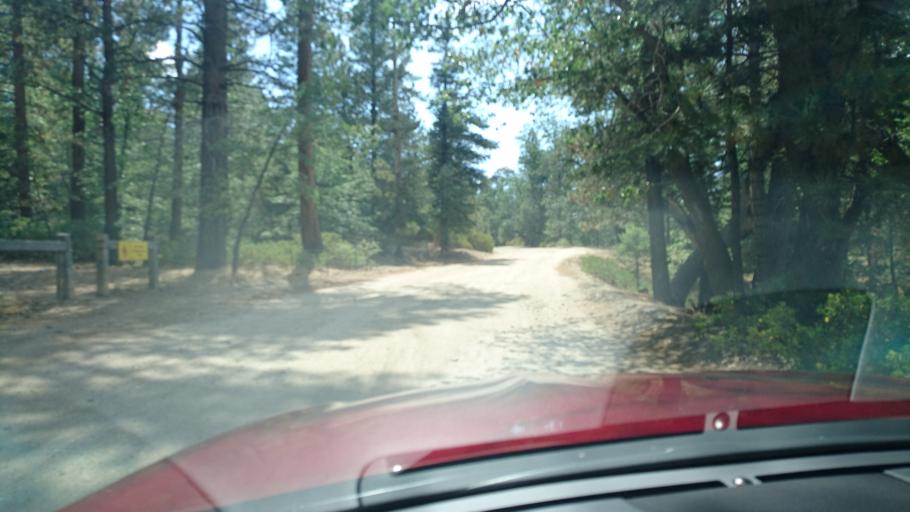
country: US
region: California
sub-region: San Bernardino County
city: Big Bear Lake
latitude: 34.2357
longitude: -116.8764
